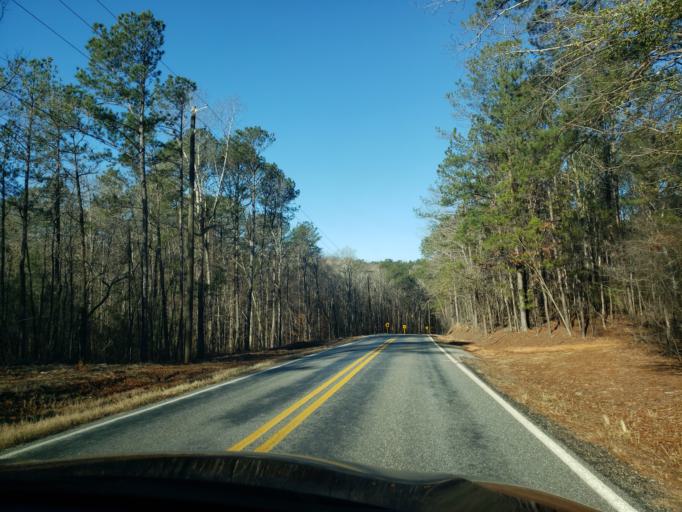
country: US
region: Alabama
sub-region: Elmore County
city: Tallassee
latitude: 32.6733
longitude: -85.8942
